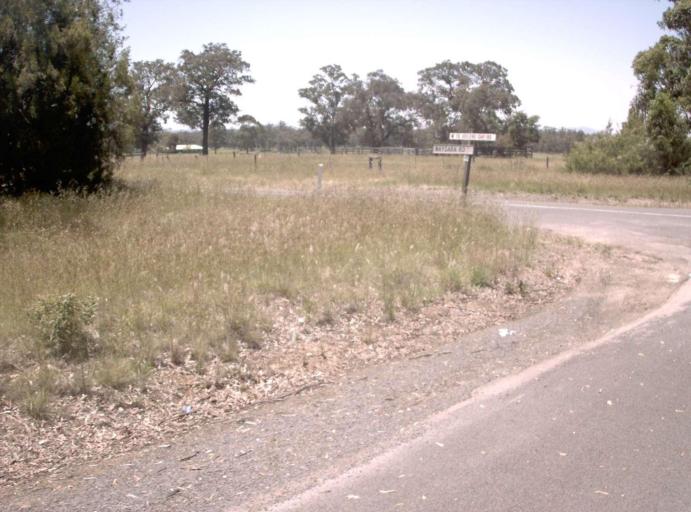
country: AU
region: Victoria
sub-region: East Gippsland
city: Lakes Entrance
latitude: -37.7540
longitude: 148.3228
